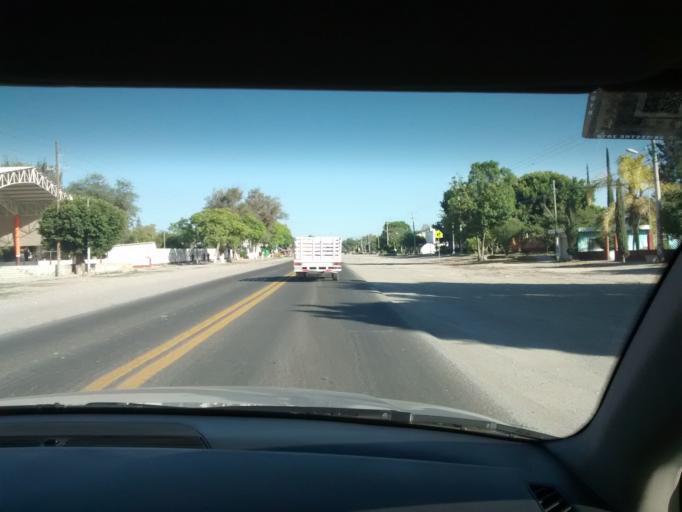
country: MX
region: Puebla
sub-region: Tehuacan
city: Magdalena Cuayucatepec
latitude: 18.5119
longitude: -97.4936
